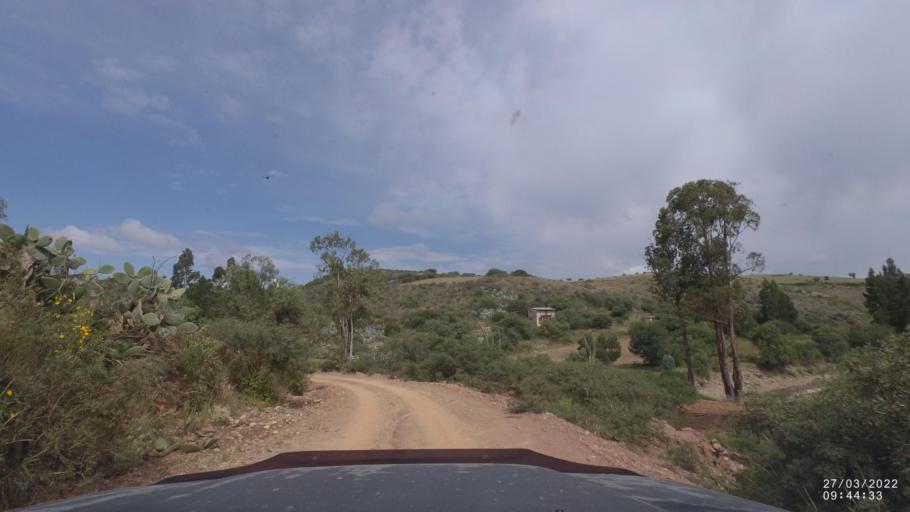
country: BO
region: Cochabamba
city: Cliza
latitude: -17.7495
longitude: -65.9109
